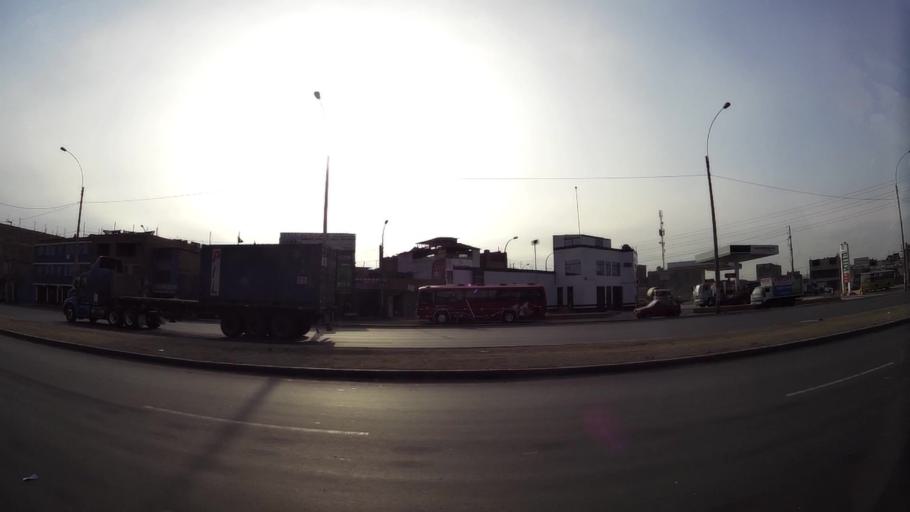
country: PE
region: Lima
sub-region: Lima
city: Independencia
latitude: -11.9899
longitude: -77.1063
